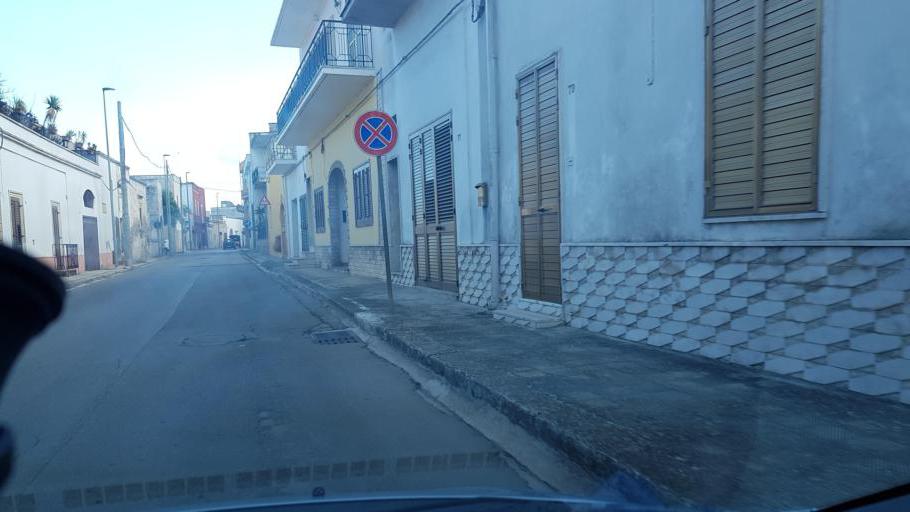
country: IT
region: Apulia
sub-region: Provincia di Lecce
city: Veglie
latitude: 40.3373
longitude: 17.9702
